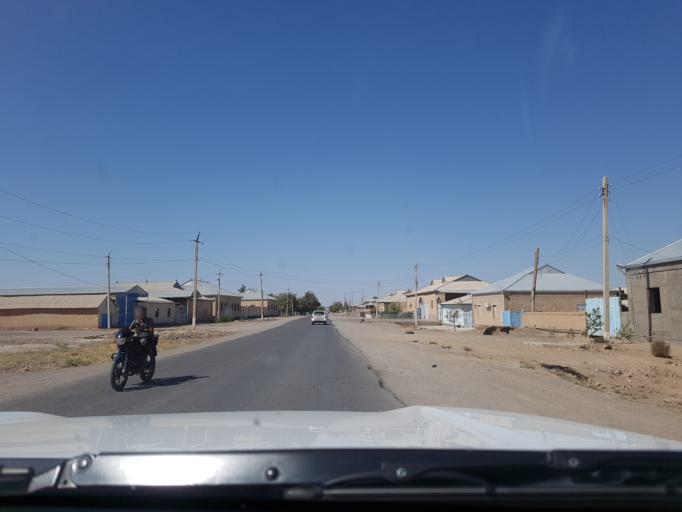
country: IR
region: Razavi Khorasan
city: Sarakhs
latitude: 36.5179
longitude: 61.2201
